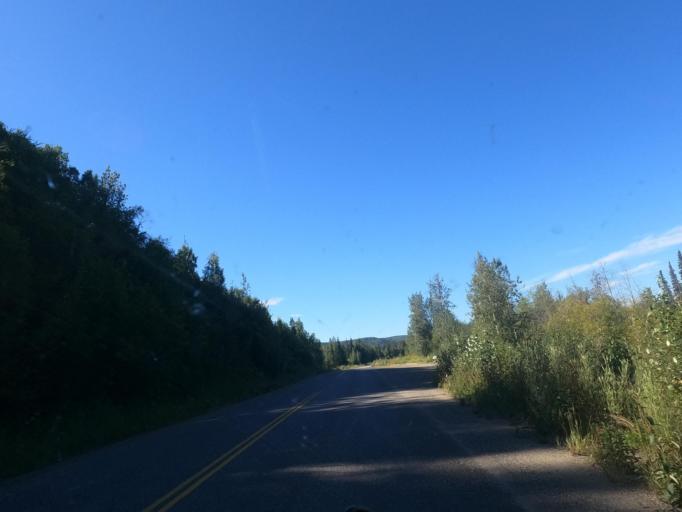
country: CA
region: Yukon
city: Dawson City
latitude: 63.9522
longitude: -138.6715
